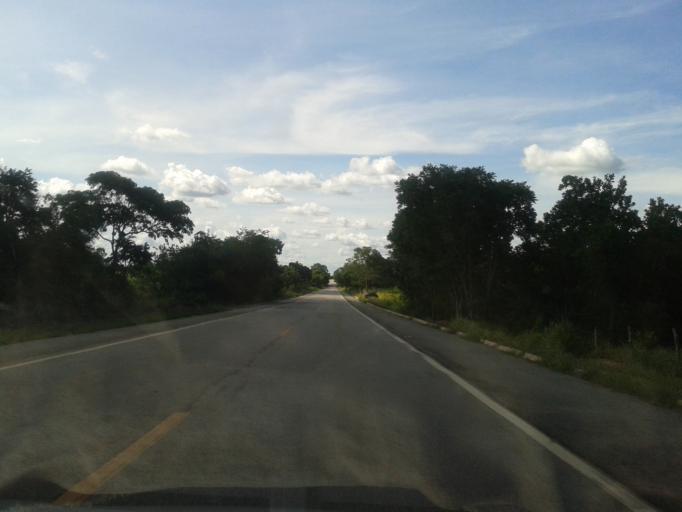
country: BR
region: Goias
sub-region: Mozarlandia
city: Mozarlandia
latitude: -15.2399
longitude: -50.5121
